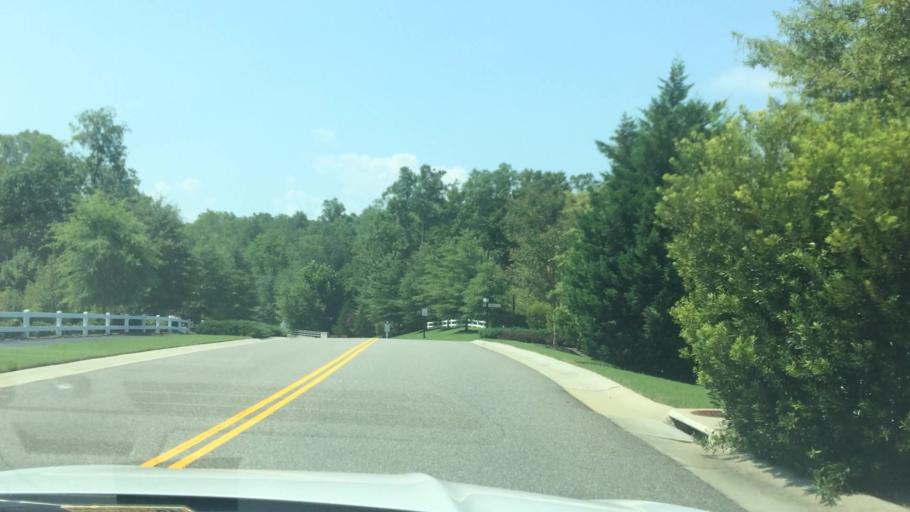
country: US
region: Virginia
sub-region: James City County
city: Williamsburg
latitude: 37.3418
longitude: -76.7773
